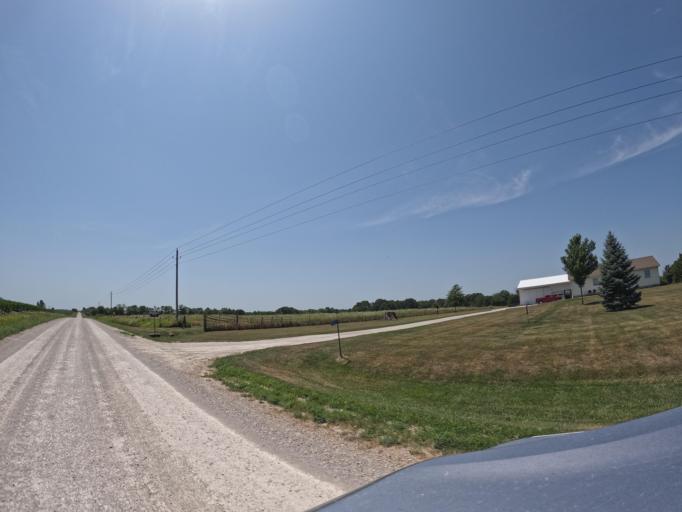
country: US
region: Iowa
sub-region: Henry County
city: Mount Pleasant
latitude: 40.9227
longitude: -91.6457
